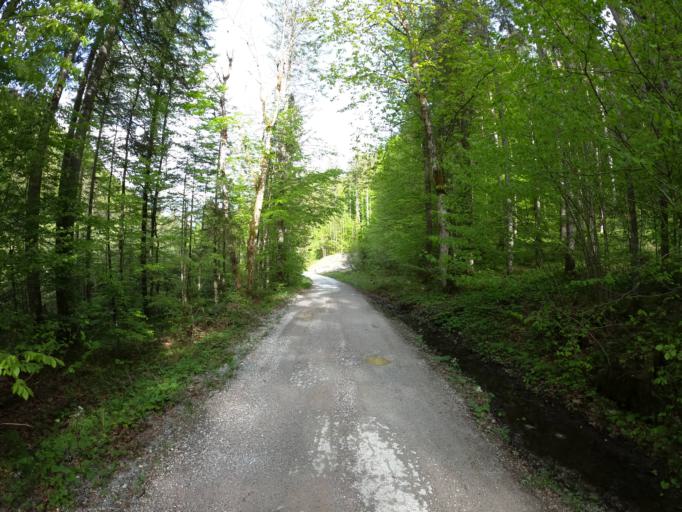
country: AT
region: Salzburg
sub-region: Politischer Bezirk Sankt Johann im Pongau
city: Werfen
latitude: 47.4768
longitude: 13.1312
